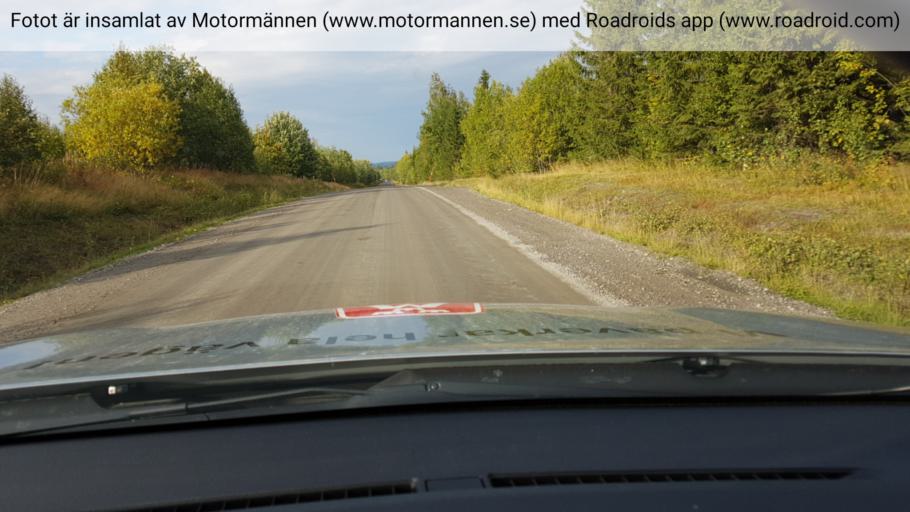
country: SE
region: Jaemtland
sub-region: Stroemsunds Kommun
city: Stroemsund
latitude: 64.0082
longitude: 15.8151
